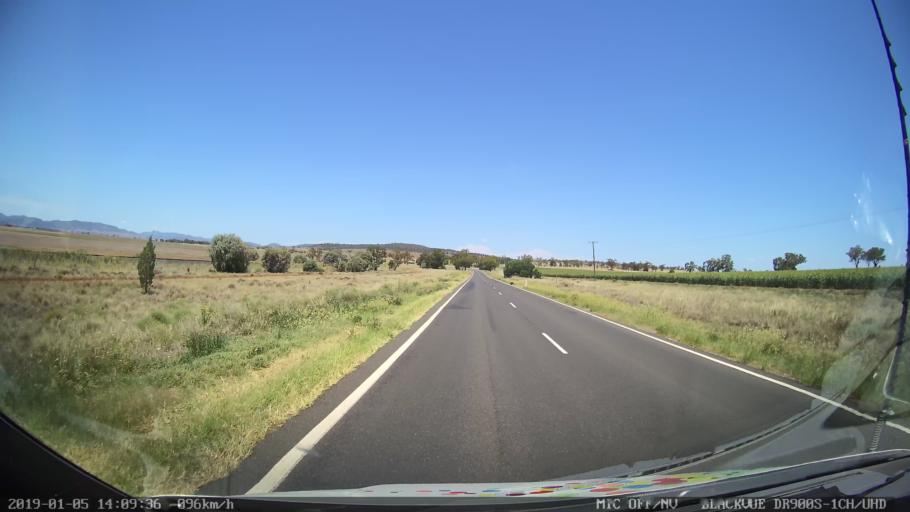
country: AU
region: New South Wales
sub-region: Gunnedah
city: Gunnedah
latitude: -31.2438
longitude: 150.4294
